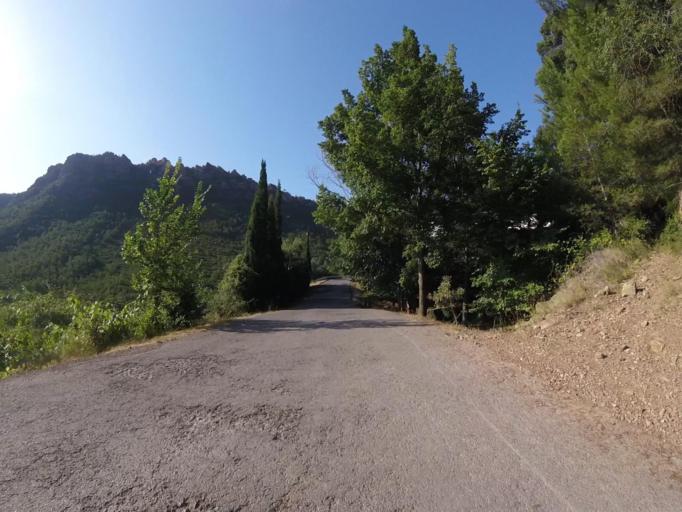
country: ES
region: Valencia
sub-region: Provincia de Castello
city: Benicassim
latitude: 40.0829
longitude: 0.0529
